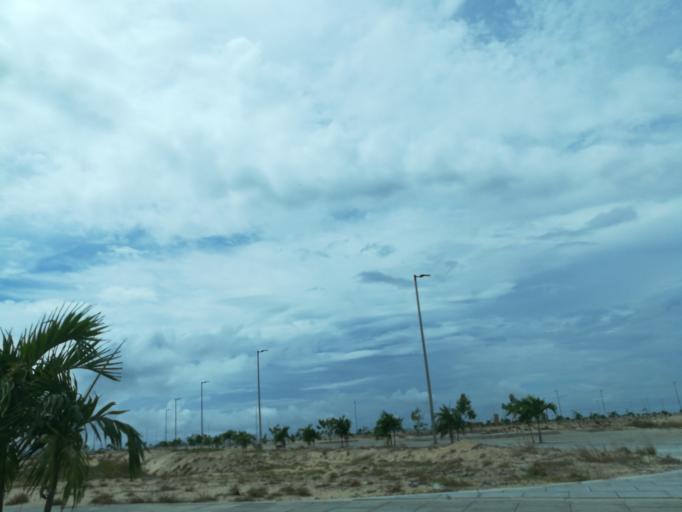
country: NG
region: Lagos
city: Lagos
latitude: 6.4108
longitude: 3.4126
